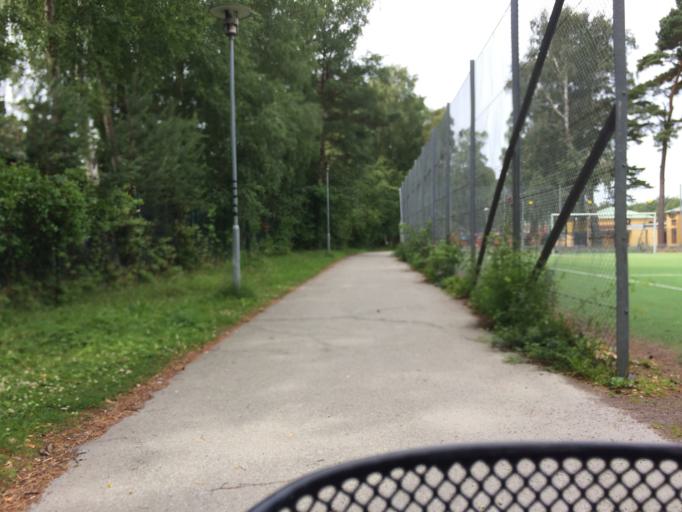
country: SE
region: Skane
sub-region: Vellinge Kommun
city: Ljunghusen
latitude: 55.4051
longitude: 12.9251
